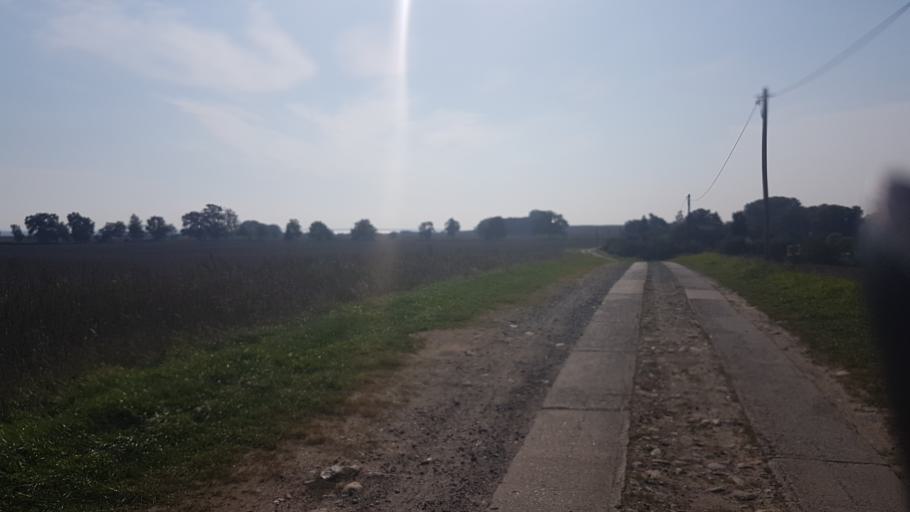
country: DE
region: Mecklenburg-Vorpommern
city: Putbus
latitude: 54.3248
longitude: 13.4552
